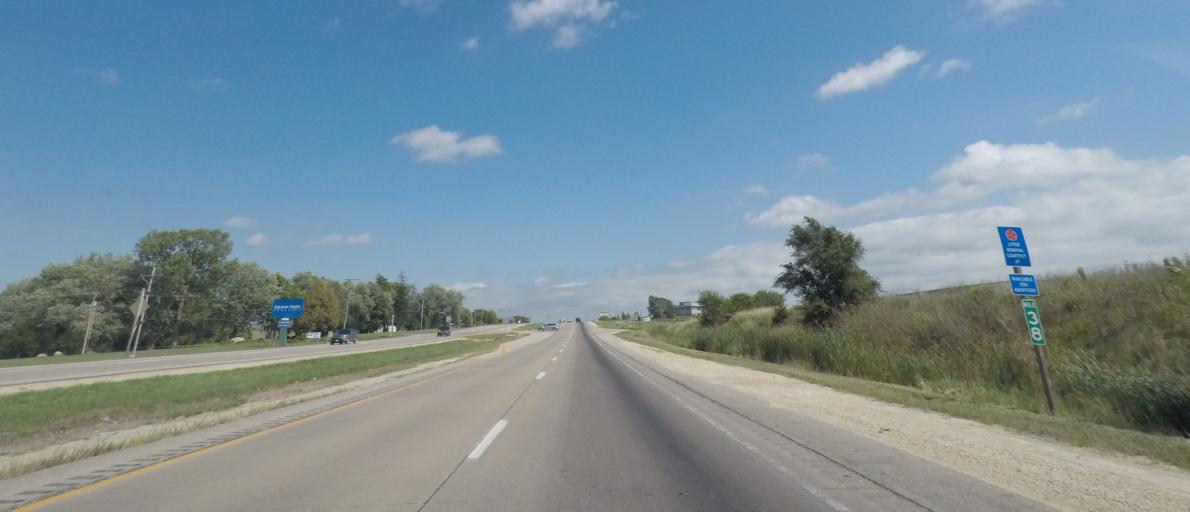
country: US
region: Iowa
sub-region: Linn County
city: Marion
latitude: 42.0356
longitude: -91.5470
